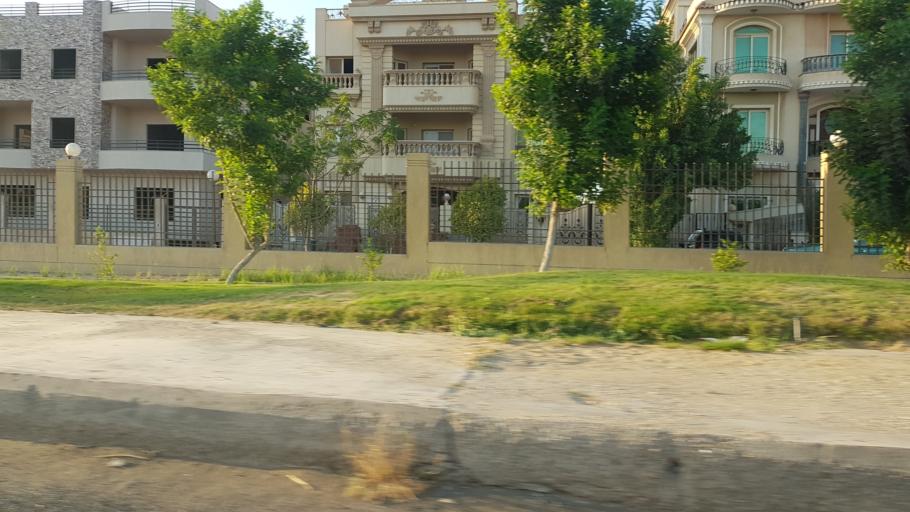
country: EG
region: Muhafazat al Qalyubiyah
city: Al Khankah
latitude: 30.0631
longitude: 31.4340
